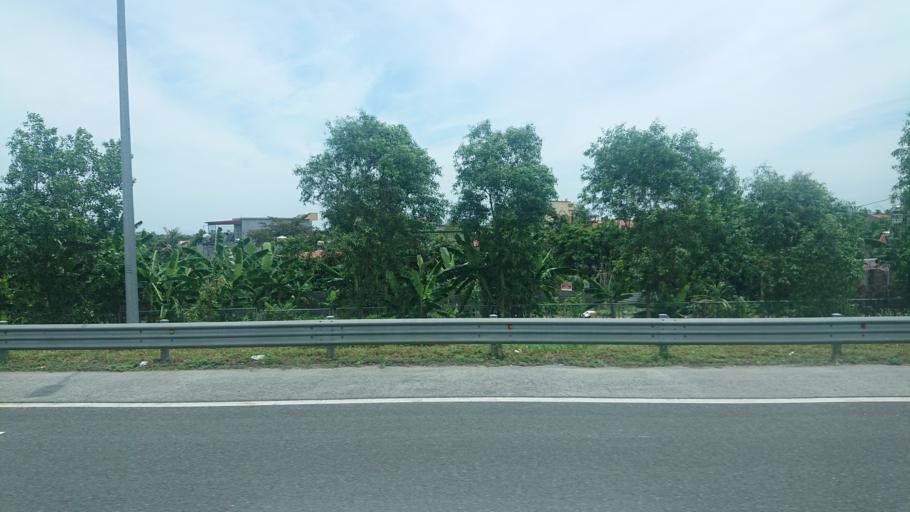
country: VN
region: Hai Phong
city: An Lao
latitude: 20.8043
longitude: 106.5221
